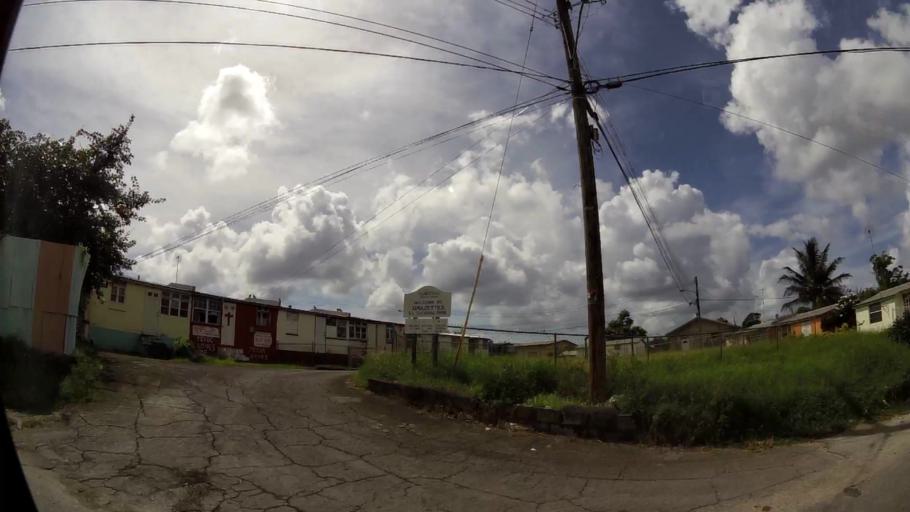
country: BB
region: Saint Michael
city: Bridgetown
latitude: 13.1291
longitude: -59.6168
